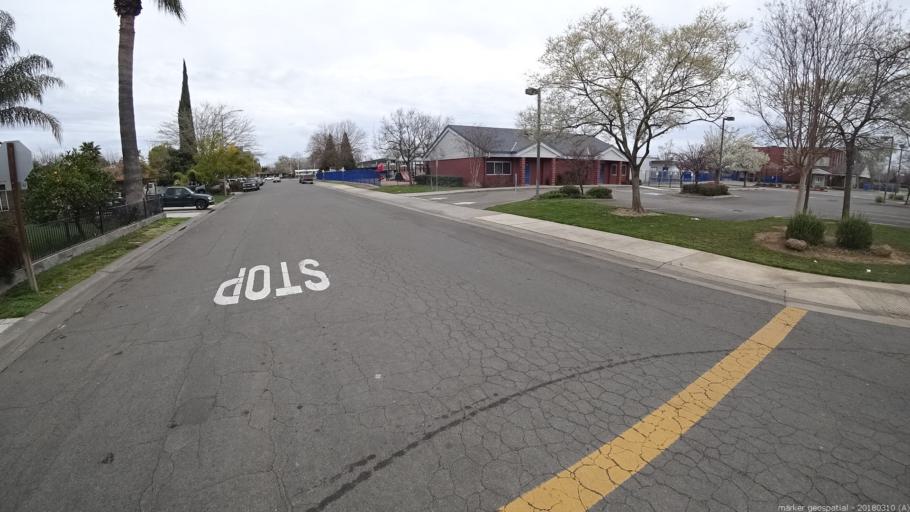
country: US
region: California
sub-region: Sacramento County
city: Florin
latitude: 38.4928
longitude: -121.4061
